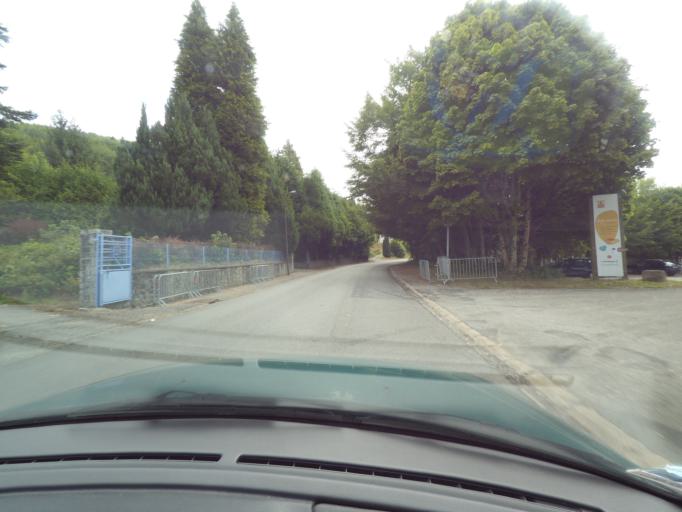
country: FR
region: Limousin
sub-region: Departement de la Haute-Vienne
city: Eymoutiers
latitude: 45.7191
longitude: 1.8336
